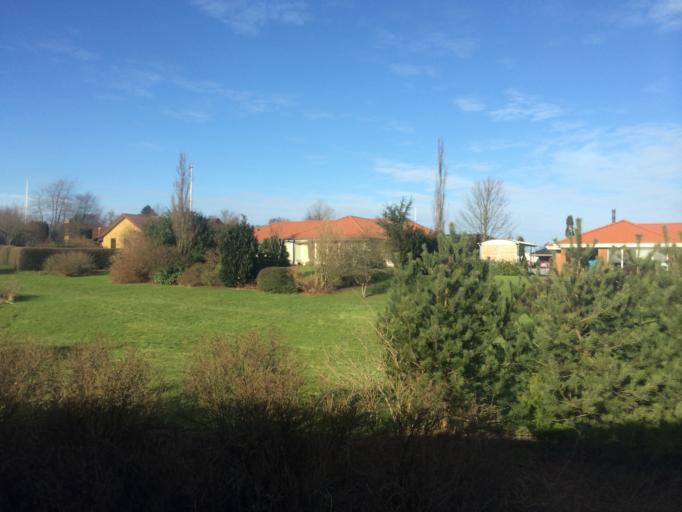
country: DK
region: South Denmark
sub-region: Vejle Kommune
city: Jelling
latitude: 55.7555
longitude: 9.4314
